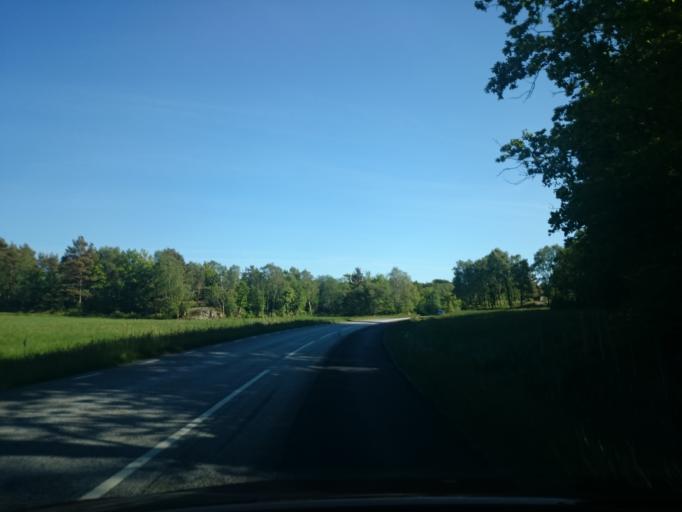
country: SE
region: Vaestra Goetaland
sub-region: Lysekils Kommun
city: Lysekil
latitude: 58.2655
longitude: 11.5384
